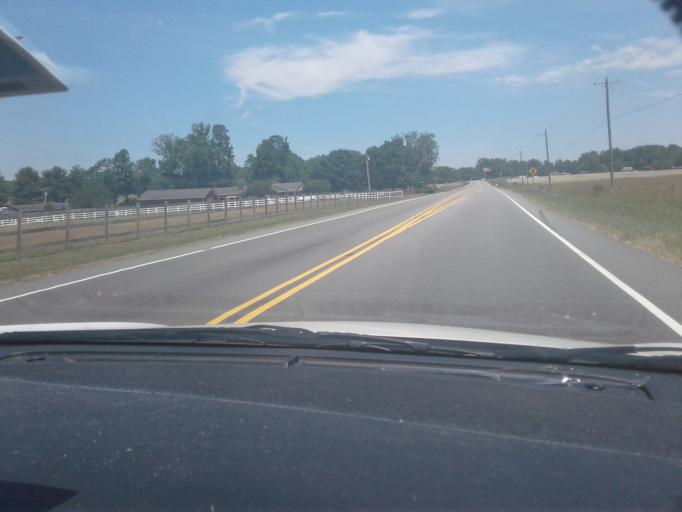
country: US
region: North Carolina
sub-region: Harnett County
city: Lillington
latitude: 35.4518
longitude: -78.8289
